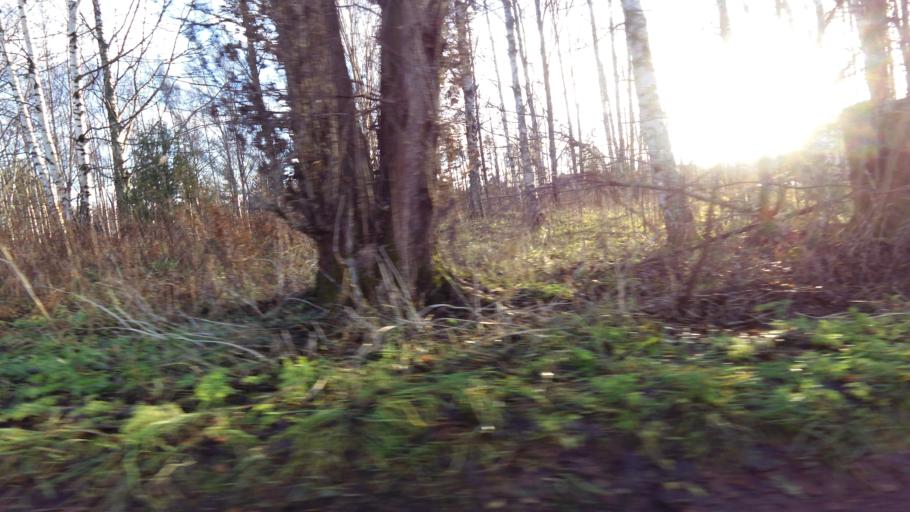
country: FI
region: Uusimaa
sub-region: Helsinki
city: Otaniemi
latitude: 60.1899
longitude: 24.8283
